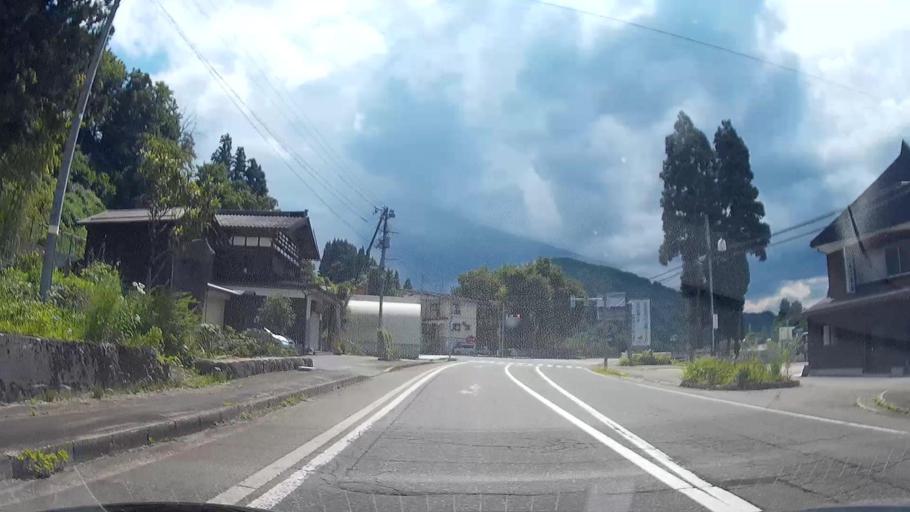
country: JP
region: Niigata
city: Tokamachi
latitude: 36.9907
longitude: 138.5884
